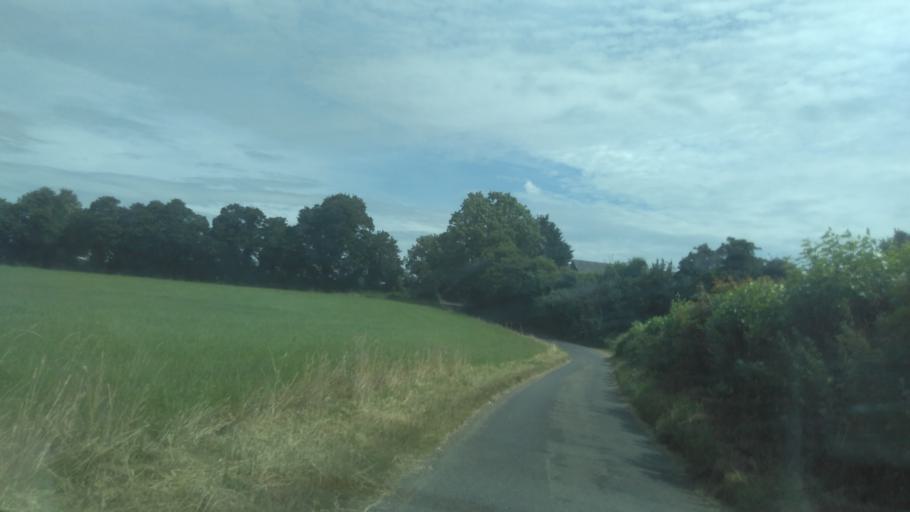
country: GB
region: England
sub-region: Kent
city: Chartham
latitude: 51.2512
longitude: 1.0020
